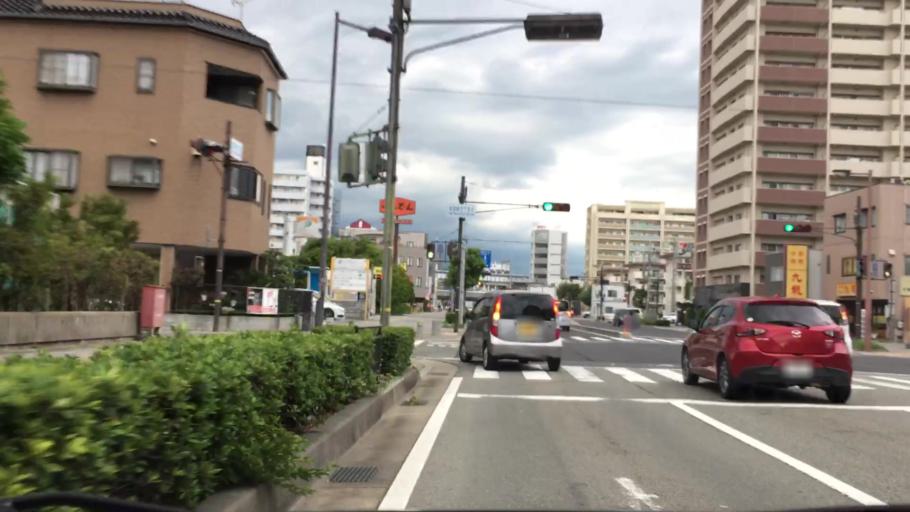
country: JP
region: Hyogo
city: Himeji
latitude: 34.8227
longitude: 134.6935
